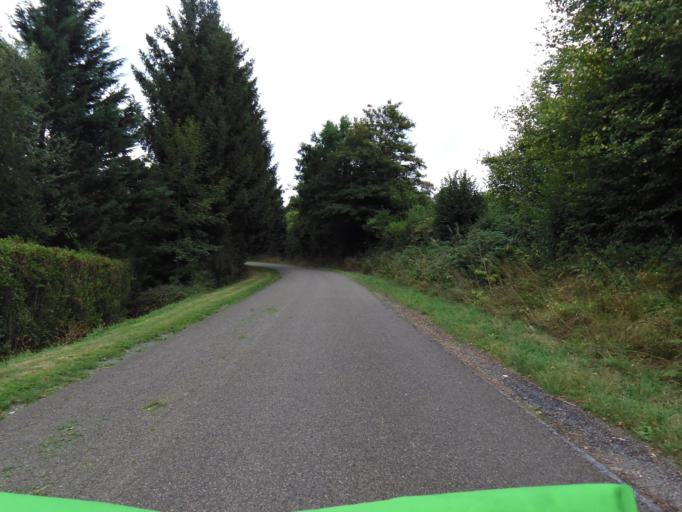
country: BE
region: Wallonia
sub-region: Province de Namur
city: Bievre
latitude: 49.8951
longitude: 5.0066
